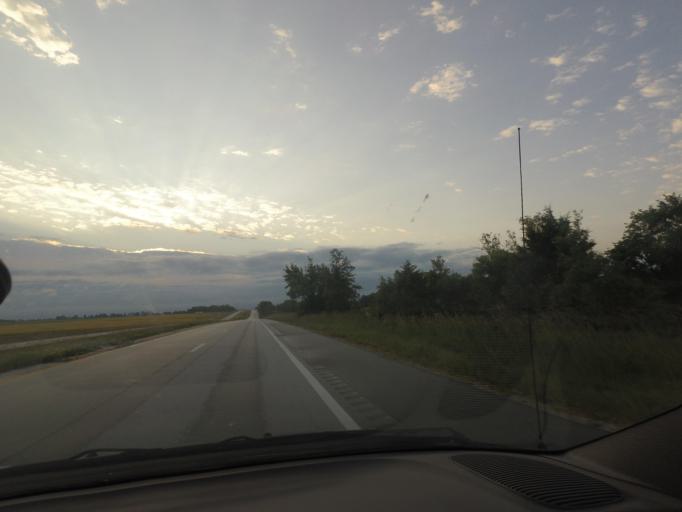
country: US
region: Missouri
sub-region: Shelby County
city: Shelbina
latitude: 39.7217
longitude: -92.1600
